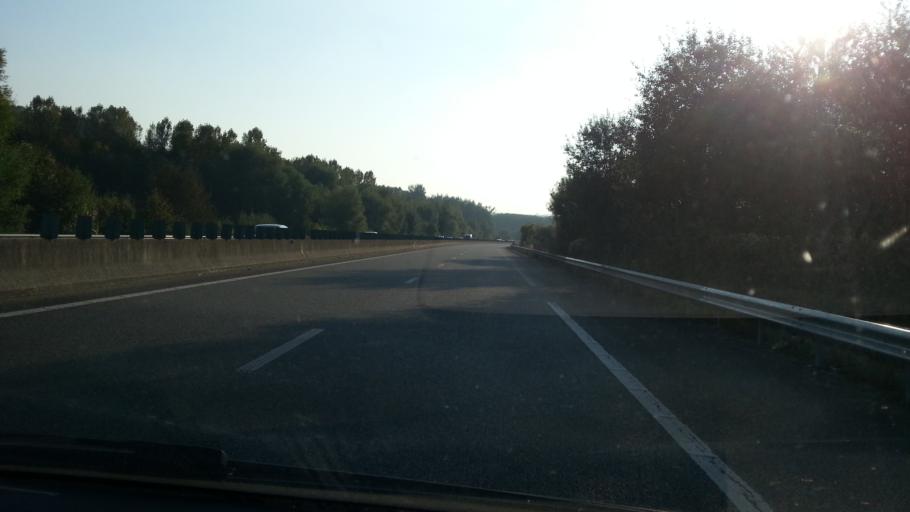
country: FR
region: Picardie
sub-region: Departement de l'Oise
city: Coudun
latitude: 49.4697
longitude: 2.8292
